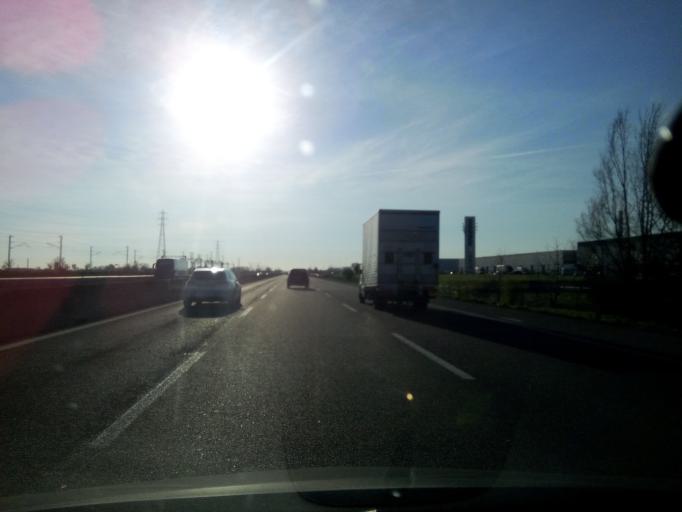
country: IT
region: Emilia-Romagna
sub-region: Provincia di Parma
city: Baganzola
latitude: 44.8525
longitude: 10.2861
